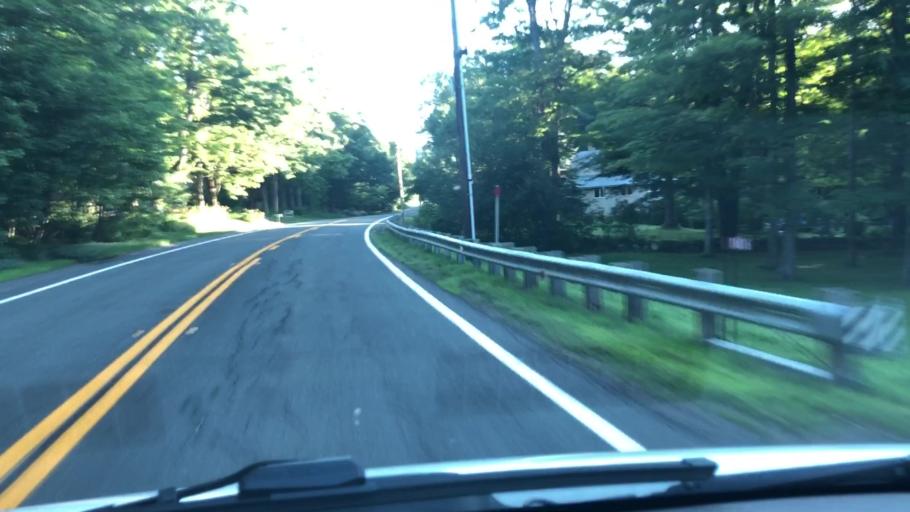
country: US
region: Massachusetts
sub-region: Hampshire County
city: Chesterfield
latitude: 42.4023
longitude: -72.9384
